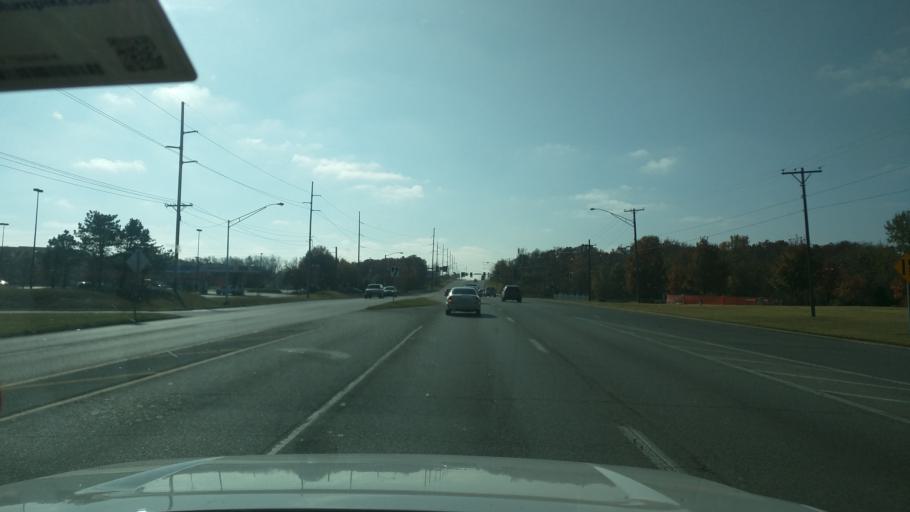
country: US
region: Oklahoma
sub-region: Washington County
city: Bartlesville
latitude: 36.7419
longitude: -95.9354
